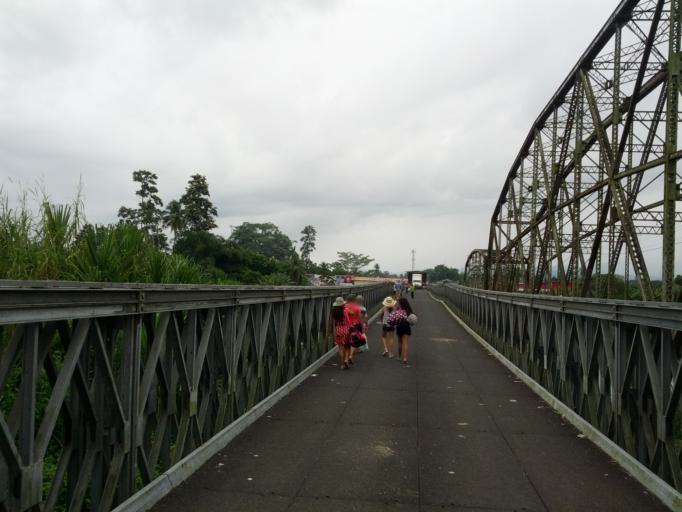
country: PA
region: Bocas del Toro
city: Guabito
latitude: 9.5004
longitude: -82.6138
